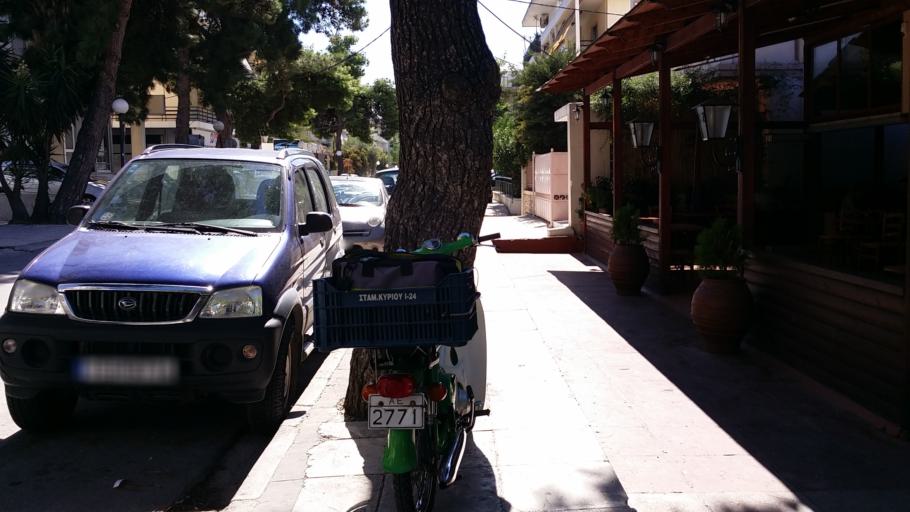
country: GR
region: Attica
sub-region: Nomarchia Athinas
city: Metamorfosi
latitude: 38.0586
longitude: 23.7584
